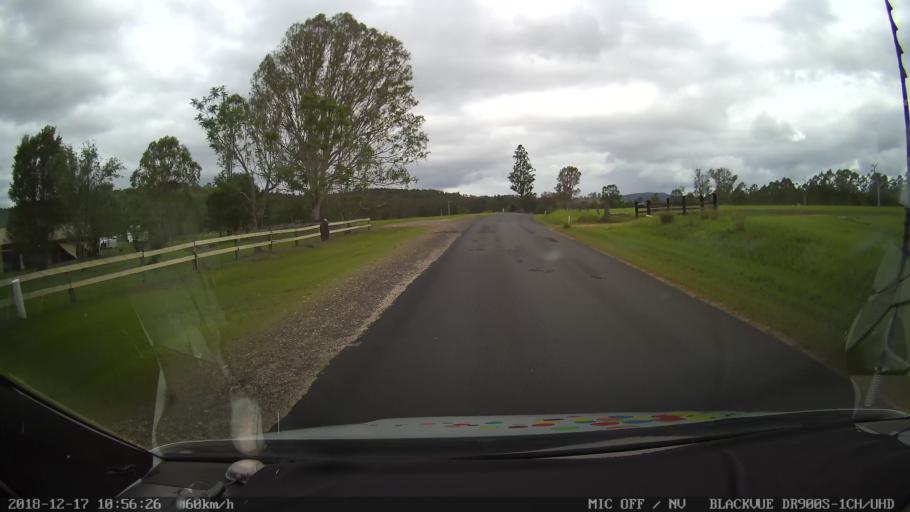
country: AU
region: New South Wales
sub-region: Richmond Valley
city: Casino
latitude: -28.8218
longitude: 152.5875
